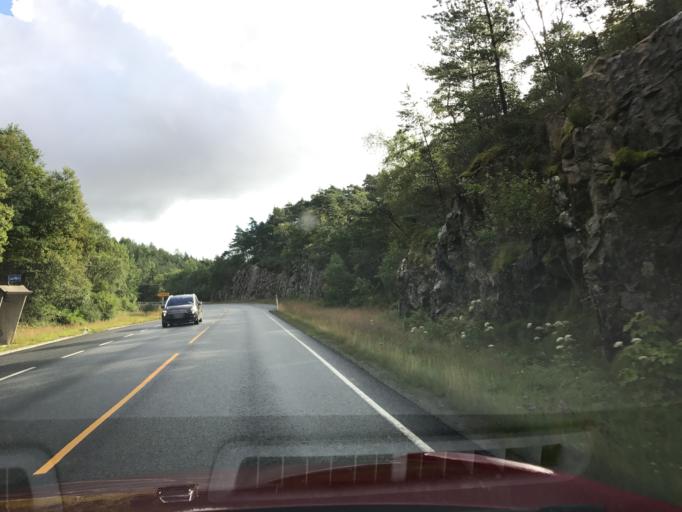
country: NO
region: Hordaland
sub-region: Bomlo
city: Mosterhamn
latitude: 59.6265
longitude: 5.4921
